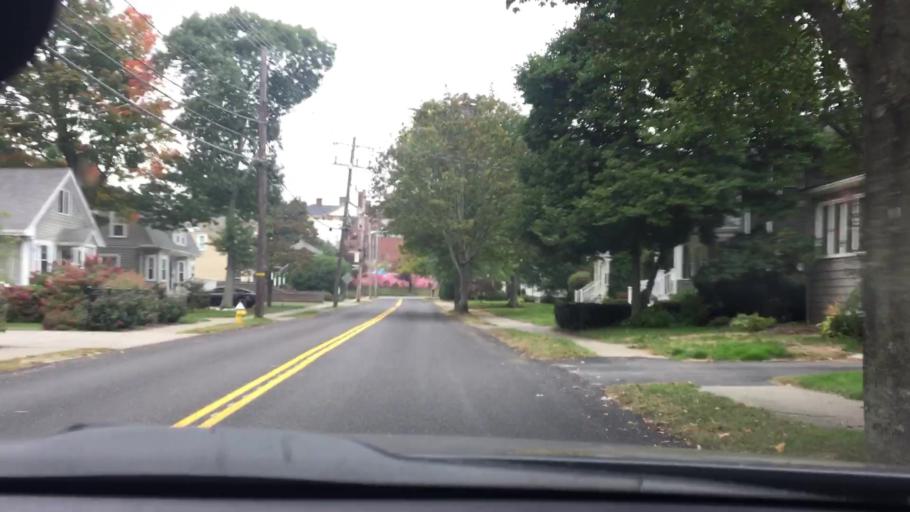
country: US
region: Massachusetts
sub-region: Norfolk County
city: Needham
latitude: 42.2867
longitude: -71.2282
